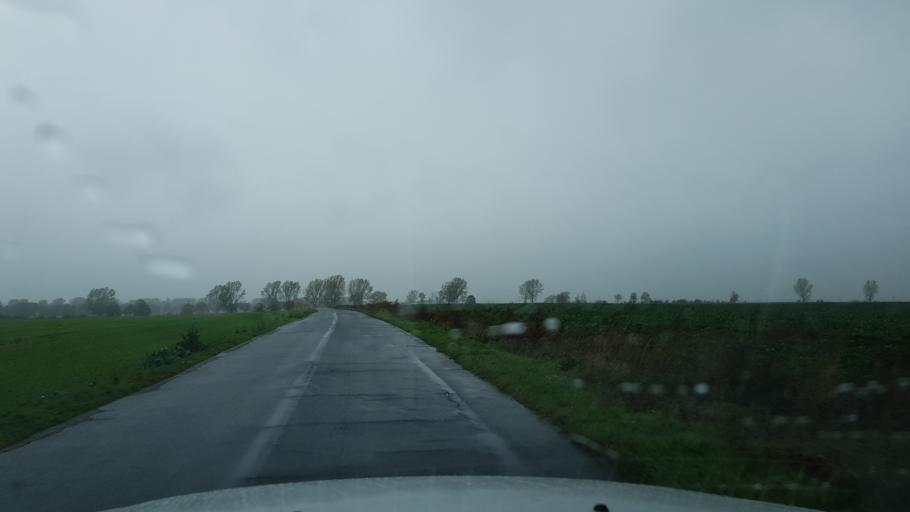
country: PL
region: West Pomeranian Voivodeship
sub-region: Powiat pyrzycki
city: Kozielice
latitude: 53.1685
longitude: 14.8208
